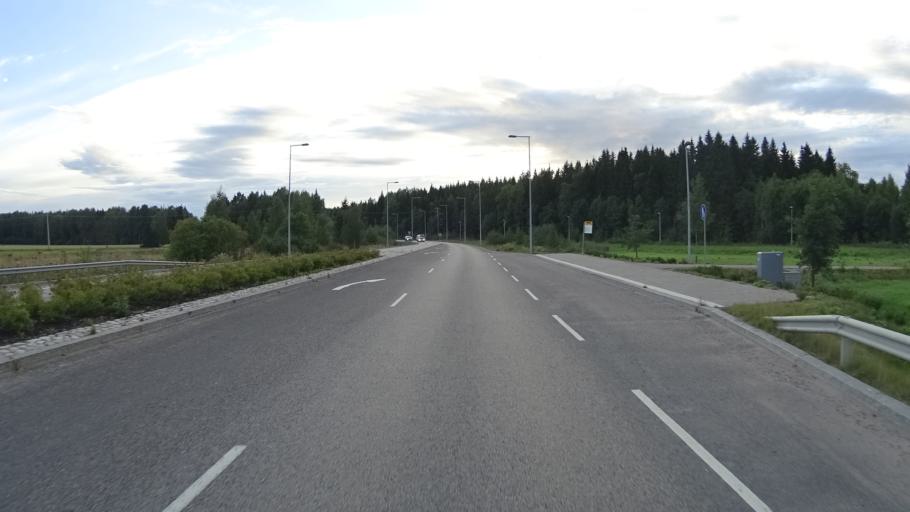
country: FI
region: Uusimaa
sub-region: Helsinki
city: Teekkarikylae
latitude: 60.3166
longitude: 24.8680
